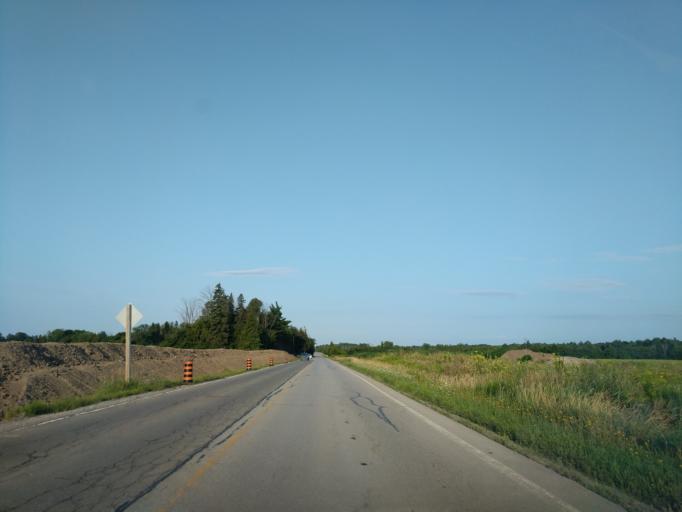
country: CA
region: Ontario
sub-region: York
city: Richmond Hill
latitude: 43.9158
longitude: -79.4023
